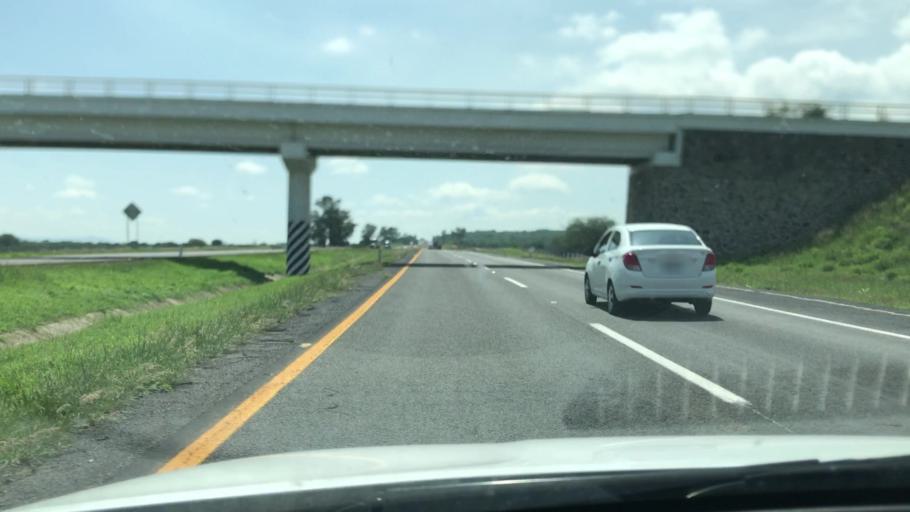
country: MX
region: Jalisco
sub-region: Poncitlan
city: Santa Cruz el Grande
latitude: 20.4424
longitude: -102.8572
